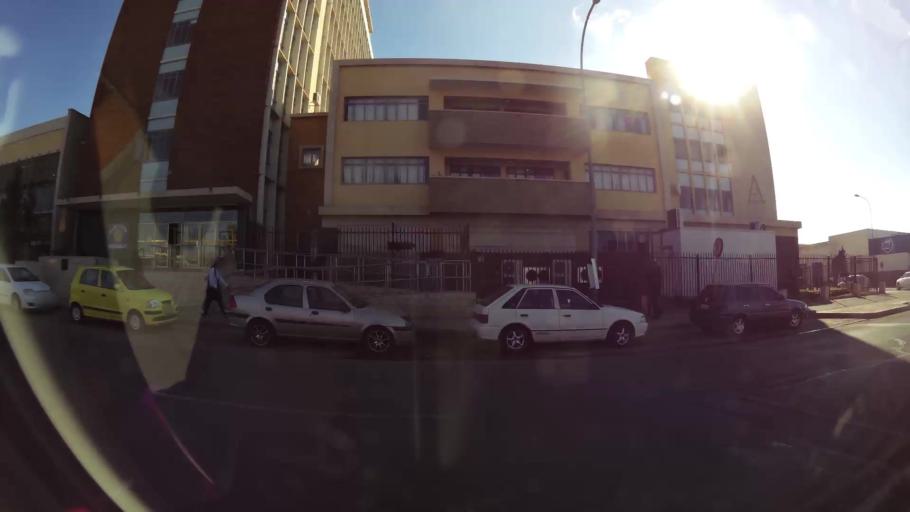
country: ZA
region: Northern Cape
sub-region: Frances Baard District Municipality
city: Kimberley
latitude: -28.7347
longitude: 24.7637
